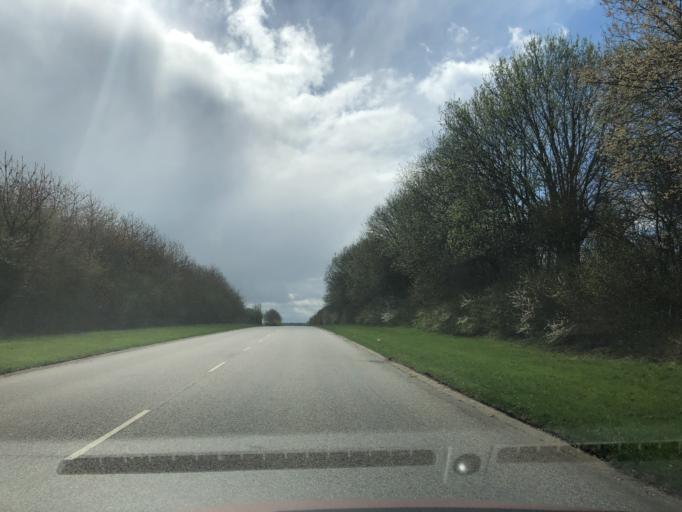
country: DK
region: South Denmark
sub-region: Kolding Kommune
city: Christiansfeld
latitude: 55.3626
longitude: 9.4958
